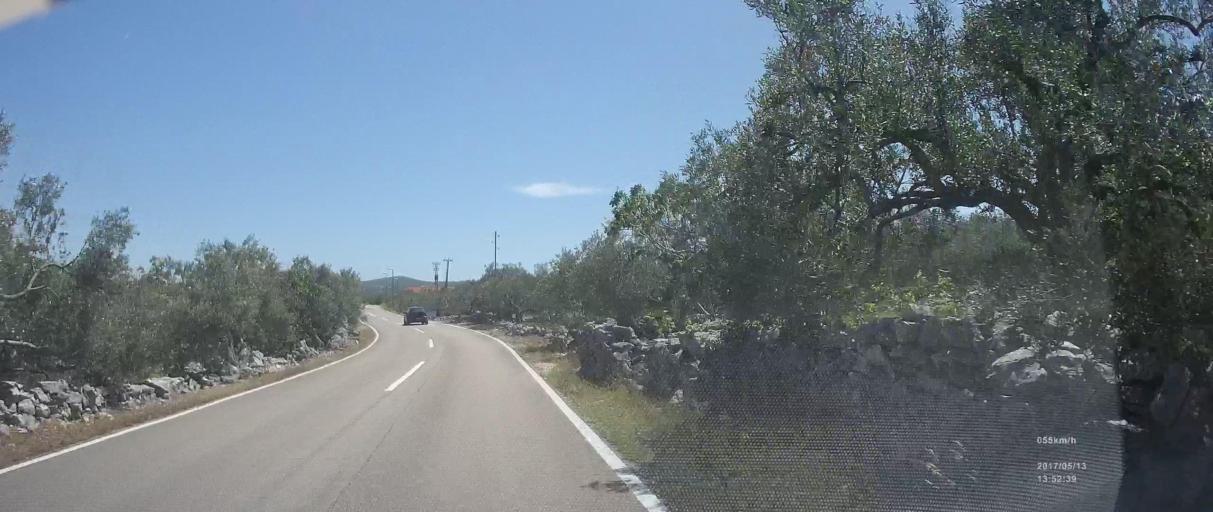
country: HR
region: Sibensko-Kniniska
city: Primosten
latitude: 43.6050
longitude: 15.9961
